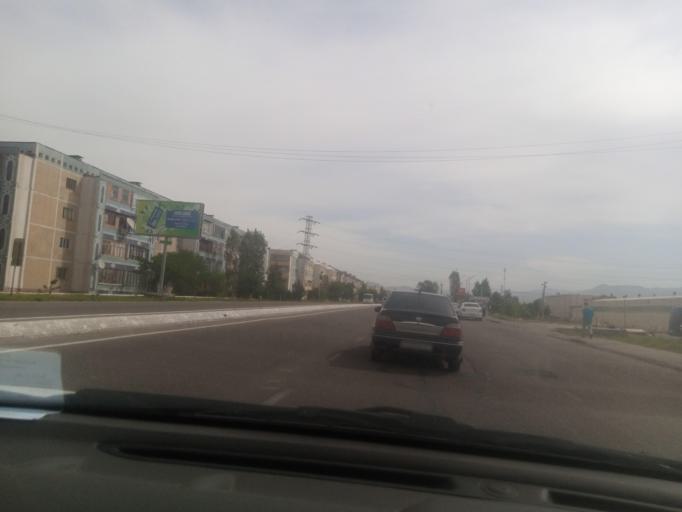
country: UZ
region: Toshkent
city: Angren
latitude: 41.0104
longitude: 70.0984
